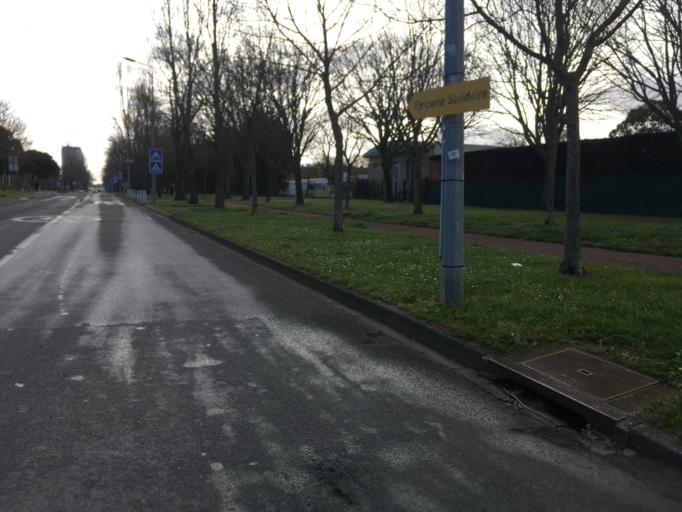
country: FR
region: Poitou-Charentes
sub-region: Departement de la Charente-Maritime
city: La Rochelle
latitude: 46.1682
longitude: -1.1868
